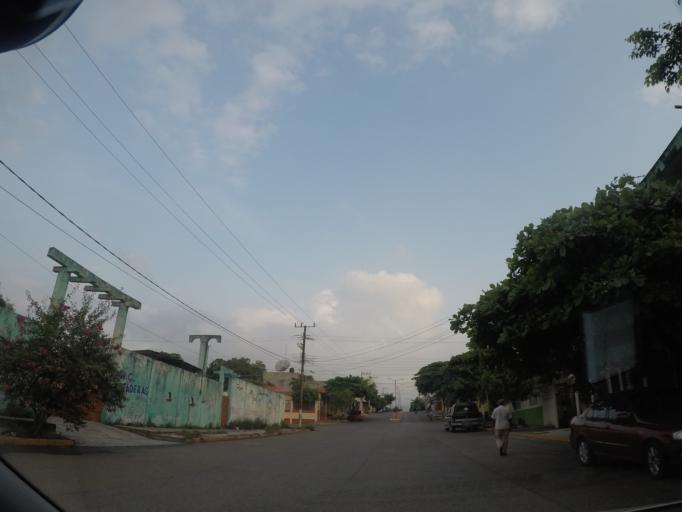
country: MX
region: Oaxaca
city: Matias Romero
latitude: 16.8752
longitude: -95.0400
